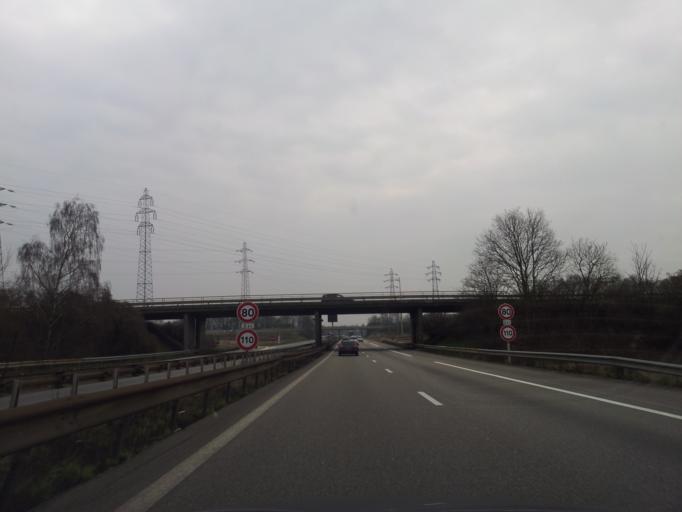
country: FR
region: Alsace
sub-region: Departement du Bas-Rhin
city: Souffelweyersheim
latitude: 48.6497
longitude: 7.7344
